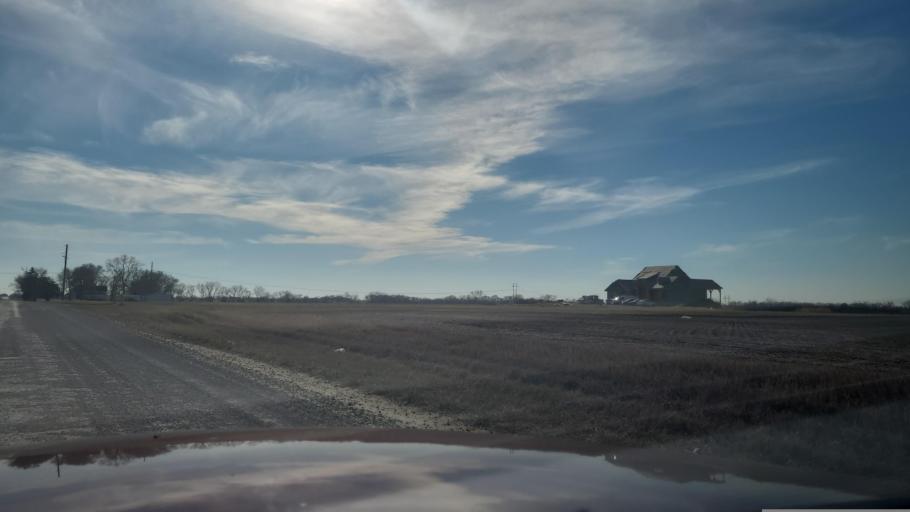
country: US
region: Kansas
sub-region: Douglas County
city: Eudora
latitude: 38.9248
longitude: -95.0748
